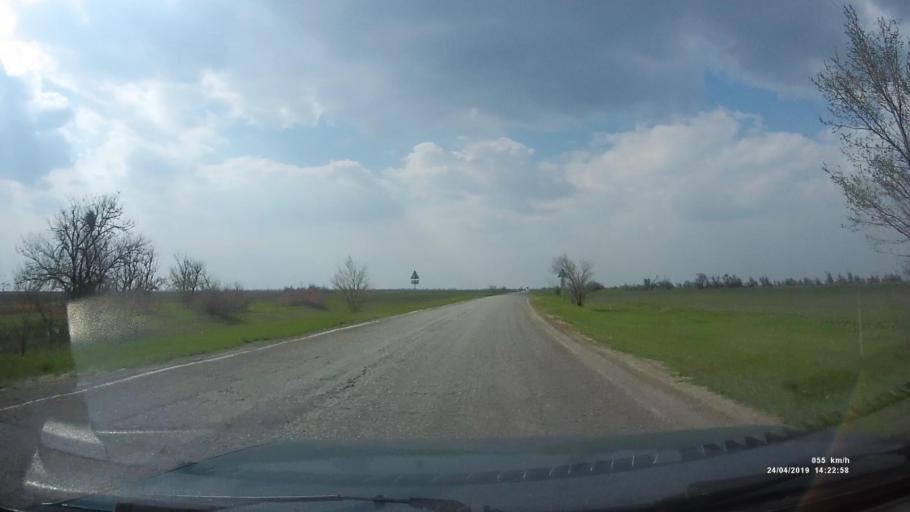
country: RU
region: Kalmykiya
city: Arshan'
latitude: 46.3185
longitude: 44.1199
